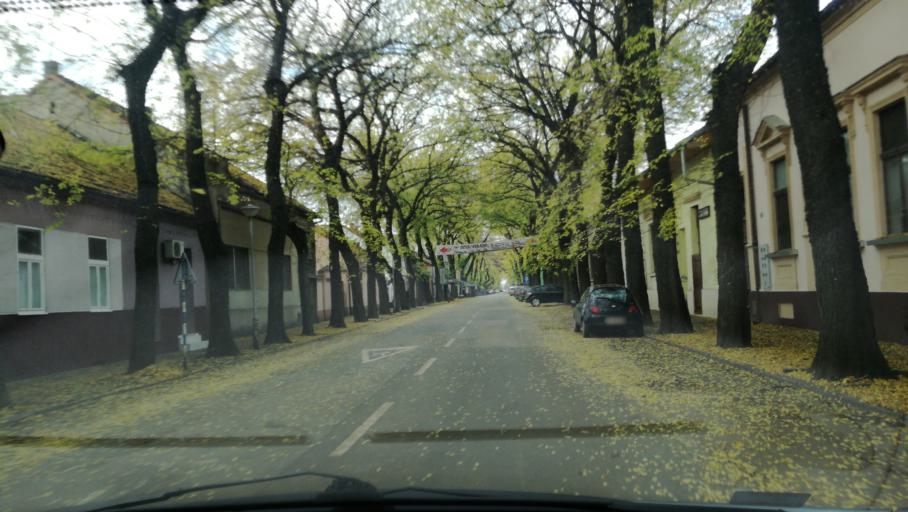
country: RS
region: Autonomna Pokrajina Vojvodina
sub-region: Severnobanatski Okrug
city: Kikinda
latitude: 45.8312
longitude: 20.4698
